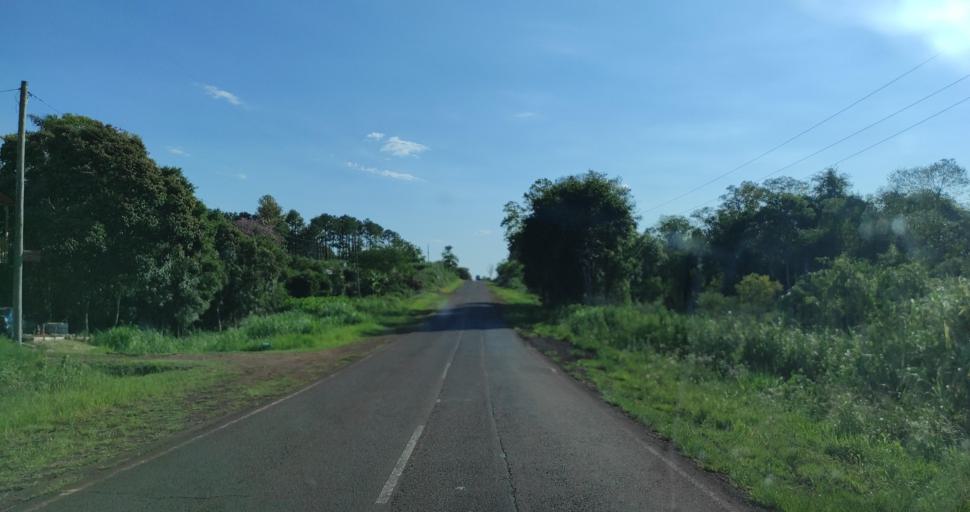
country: AR
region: Misiones
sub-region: Departamento de Eldorado
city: Eldorado
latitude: -26.3807
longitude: -54.3398
